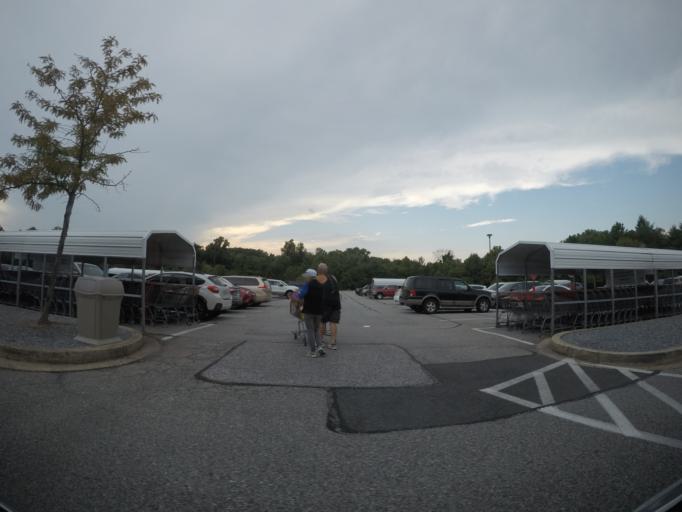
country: US
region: Maryland
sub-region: Harford County
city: Joppatowne
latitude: 39.4545
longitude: -76.3198
